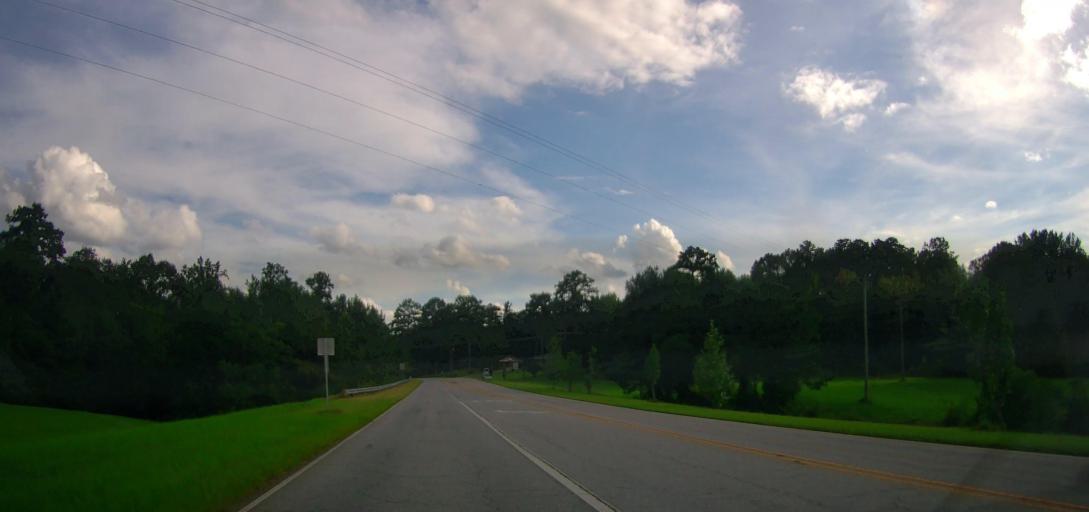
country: US
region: Alabama
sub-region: Russell County
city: Phenix City
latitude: 32.4991
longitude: -85.0013
